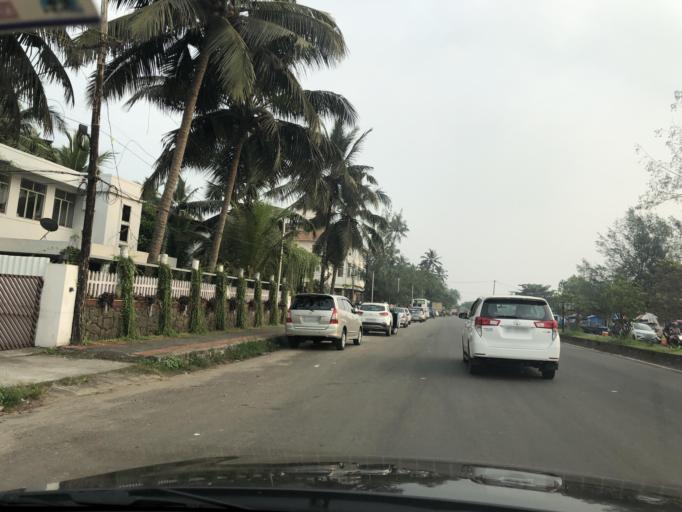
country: IN
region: Kerala
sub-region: Kozhikode
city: Kozhikode
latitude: 11.2908
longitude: 75.7587
